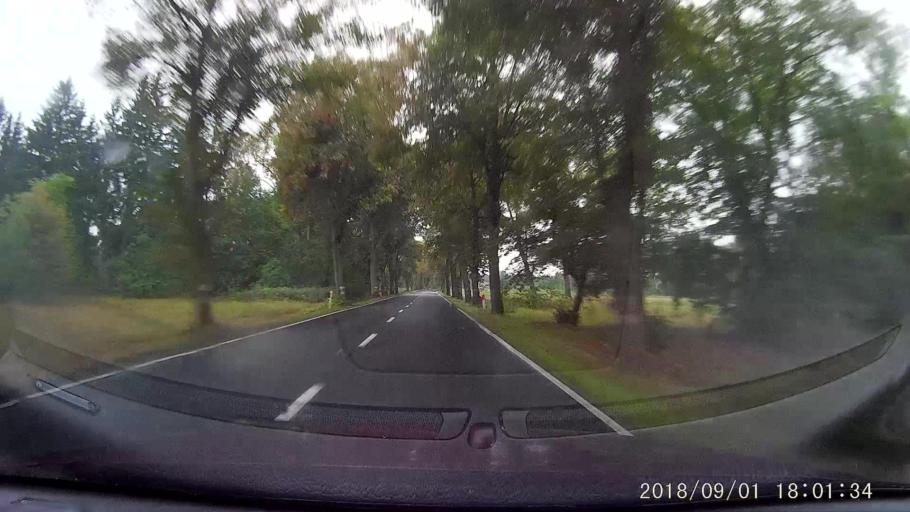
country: PL
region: Lubusz
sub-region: Powiat zaganski
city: Gozdnica
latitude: 51.3959
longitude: 15.1823
